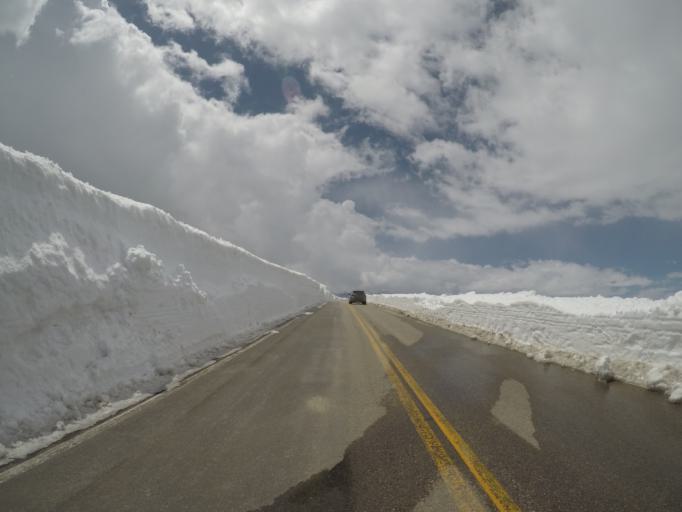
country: US
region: Montana
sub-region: Carbon County
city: Red Lodge
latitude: 44.9757
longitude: -109.4319
